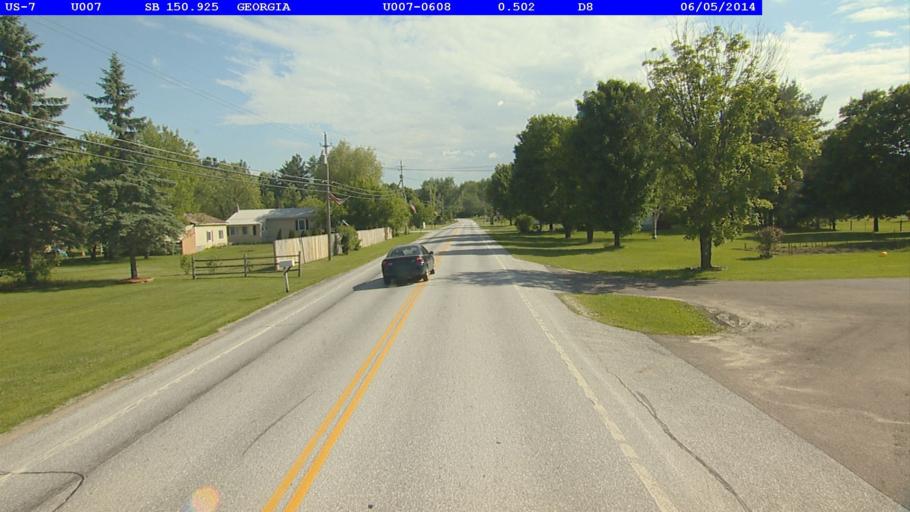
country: US
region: Vermont
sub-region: Chittenden County
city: Milton
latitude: 44.6863
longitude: -73.1104
